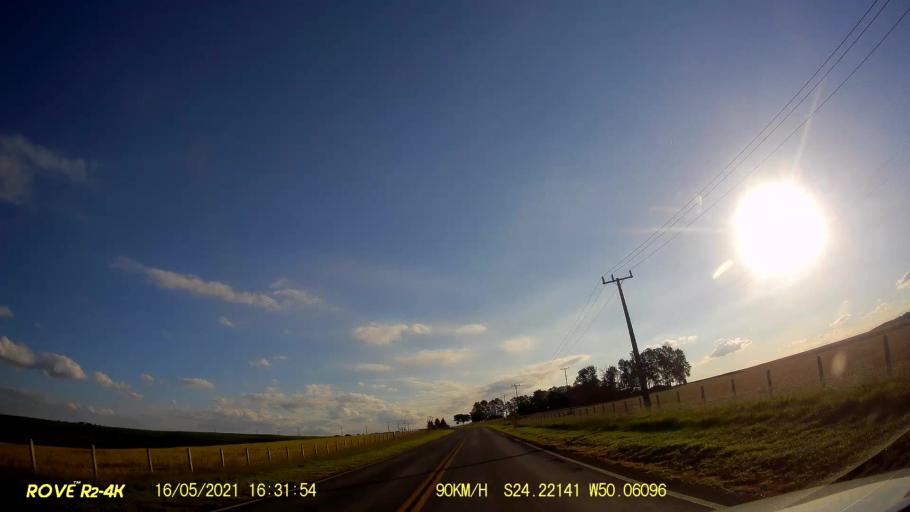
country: BR
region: Parana
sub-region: Pirai Do Sul
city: Pirai do Sul
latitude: -24.2214
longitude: -50.0613
